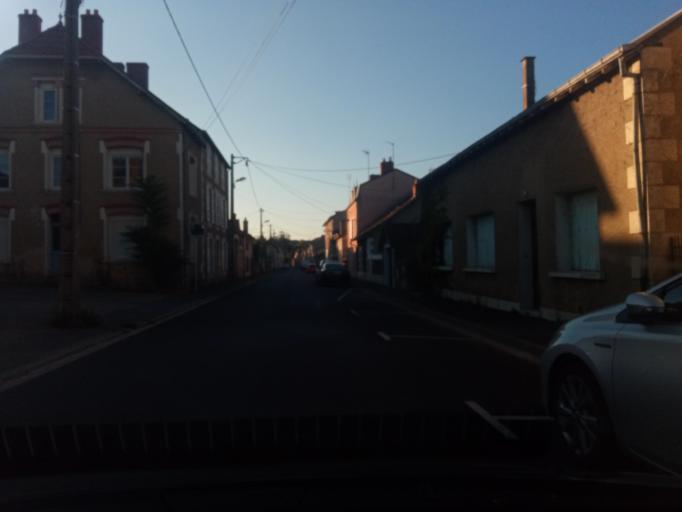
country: FR
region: Poitou-Charentes
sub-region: Departement de la Vienne
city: Montmorillon
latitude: 46.4201
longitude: 0.8708
